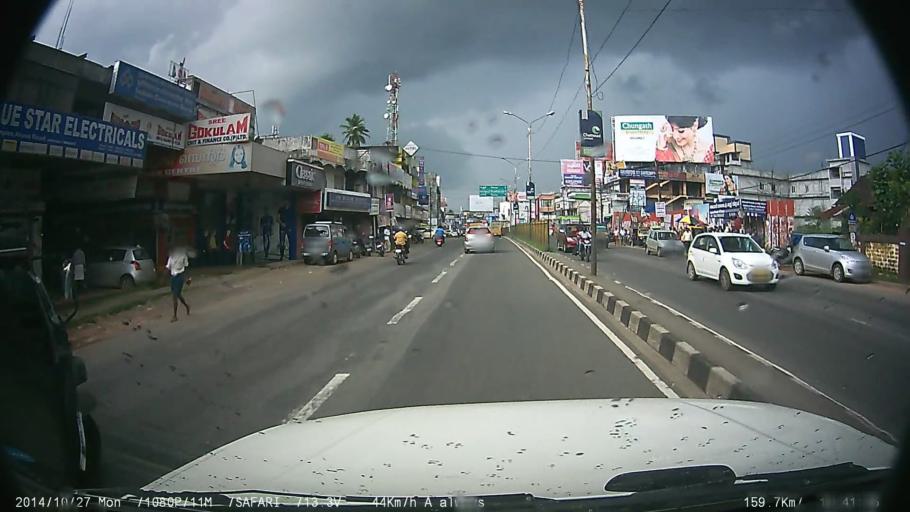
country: IN
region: Kerala
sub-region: Ernakulam
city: Angamali
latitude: 10.1909
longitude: 76.3869
